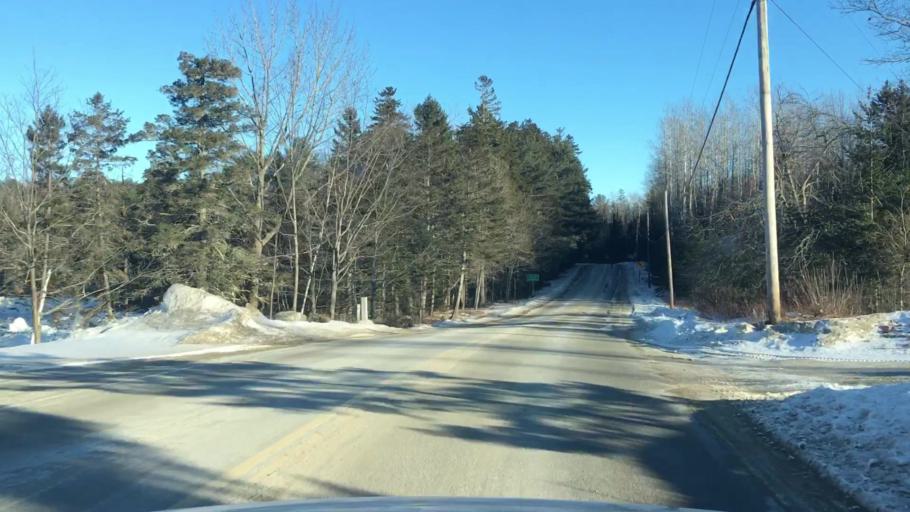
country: US
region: Maine
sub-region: Hancock County
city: Penobscot
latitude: 44.3979
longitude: -68.7035
